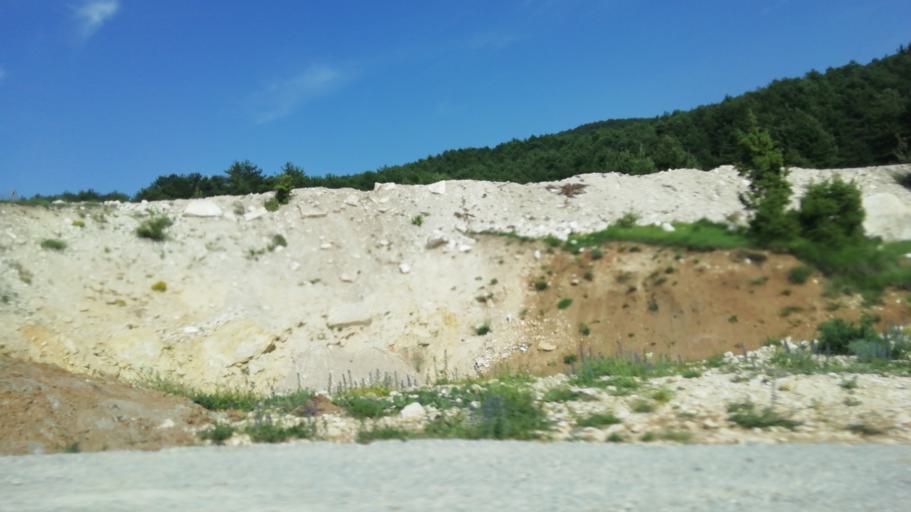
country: TR
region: Karabuk
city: Karabuk
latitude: 41.1185
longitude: 32.5804
